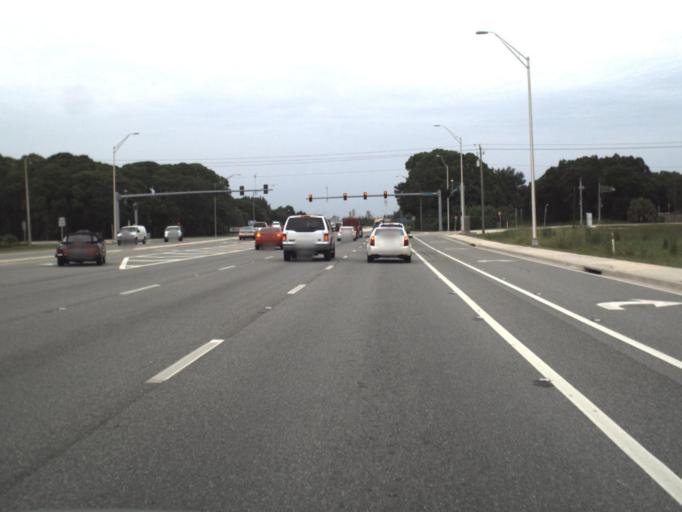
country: US
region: Florida
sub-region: Sarasota County
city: North Sarasota
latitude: 27.3802
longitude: -82.5307
